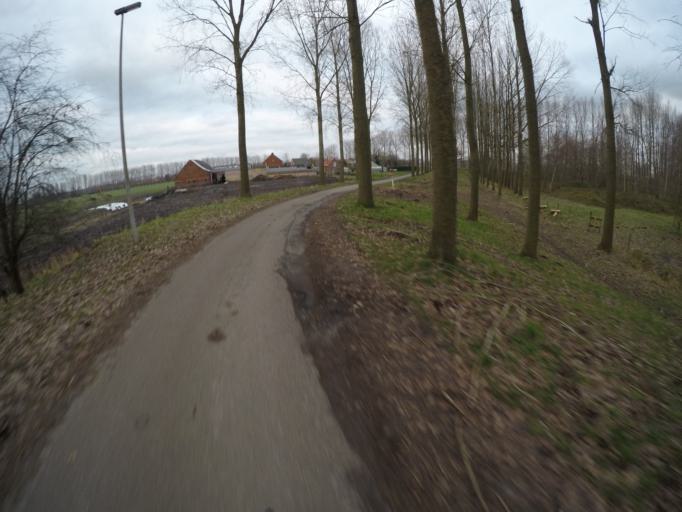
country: BE
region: Flanders
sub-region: Provincie Oost-Vlaanderen
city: Sint-Gillis-Waas
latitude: 51.2452
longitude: 4.1464
